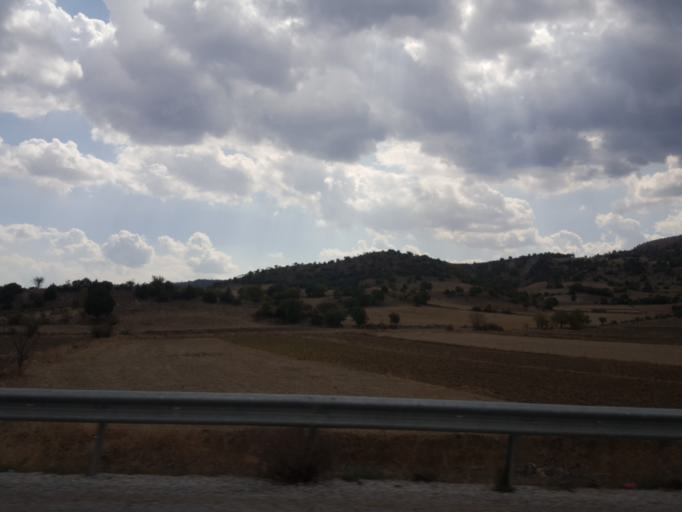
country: TR
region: Yozgat
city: Cekerek
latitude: 40.1924
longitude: 35.4249
